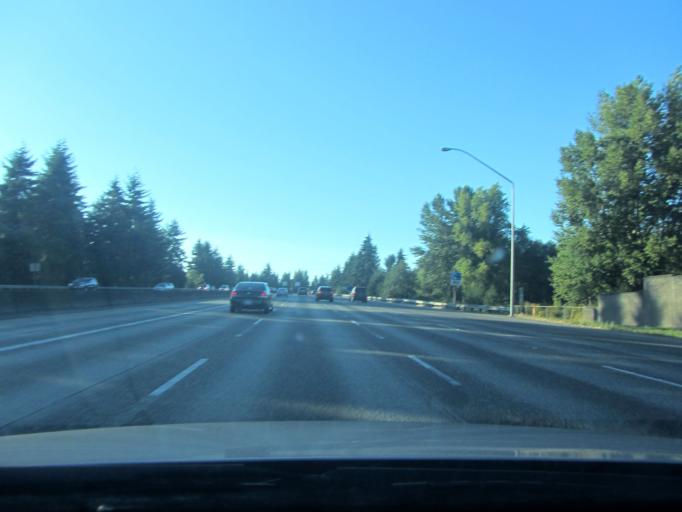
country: US
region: Washington
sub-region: King County
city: Shoreline
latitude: 47.7391
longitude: -122.3276
